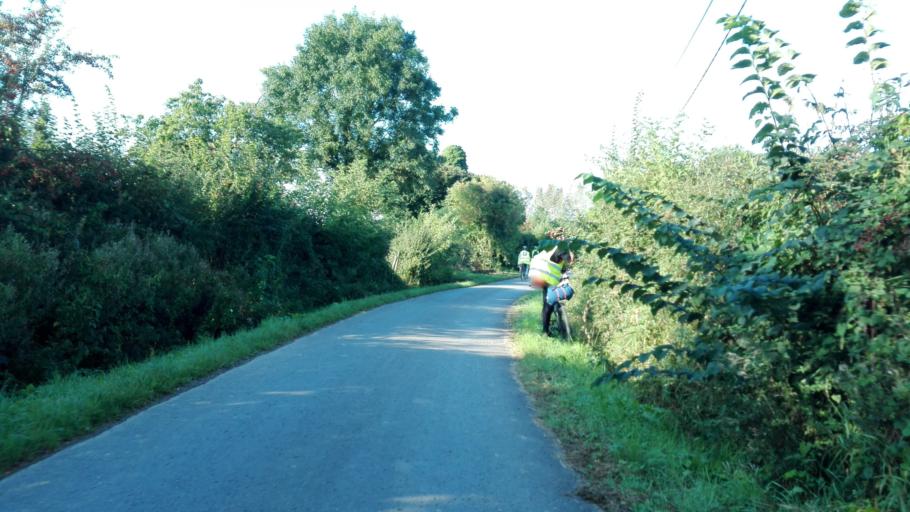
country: FR
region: Nord-Pas-de-Calais
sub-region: Departement du Pas-de-Calais
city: Eperlecques
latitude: 50.8232
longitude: 2.1662
